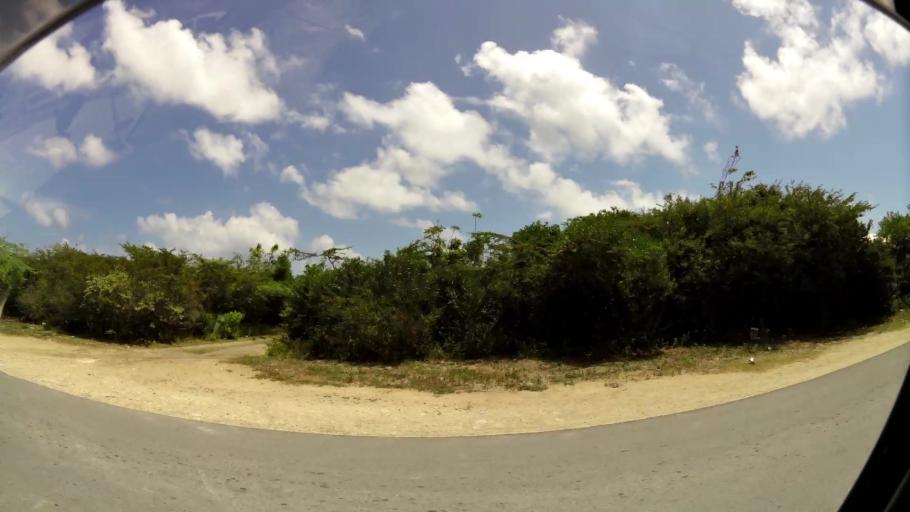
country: TC
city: Cockburn Town
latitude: 21.4615
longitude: -71.1398
